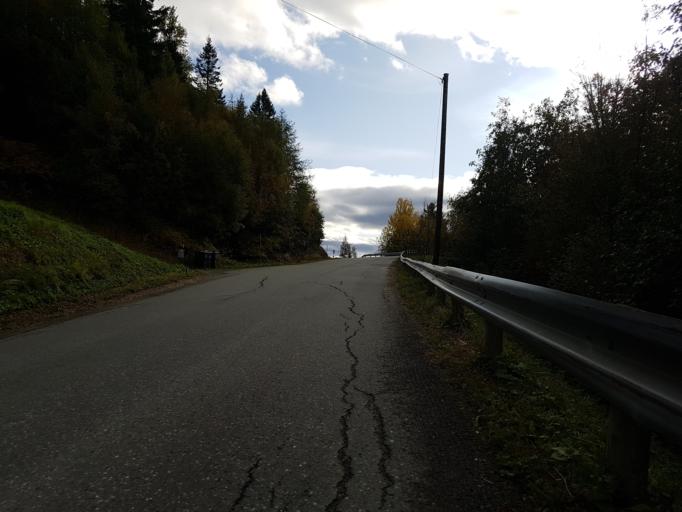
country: NO
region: Sor-Trondelag
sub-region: Klaebu
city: Klaebu
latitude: 63.3918
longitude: 10.5569
